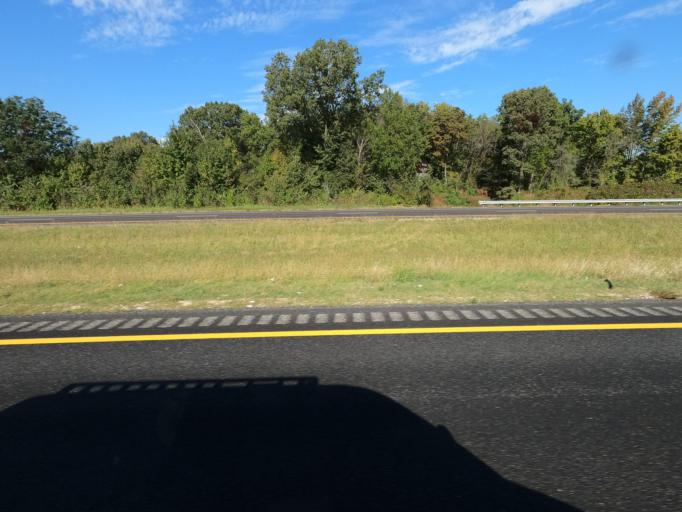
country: US
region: Tennessee
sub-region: Fayette County
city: Hickory Withe
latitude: 35.3267
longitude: -89.5616
